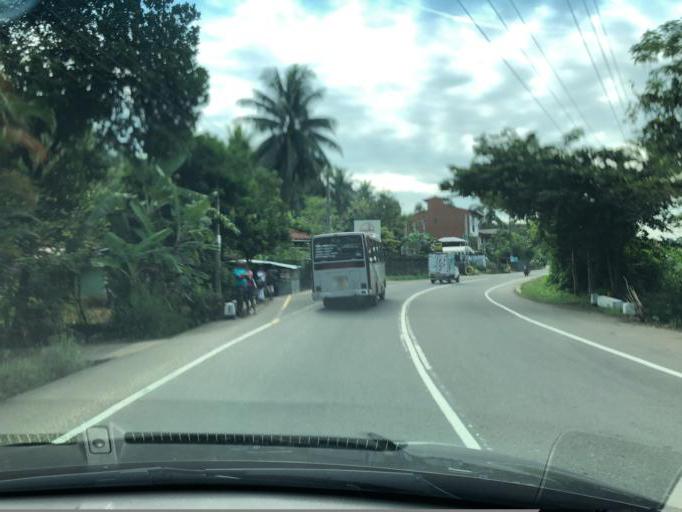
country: LK
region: Western
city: Kalutara
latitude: 6.5639
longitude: 80.0060
